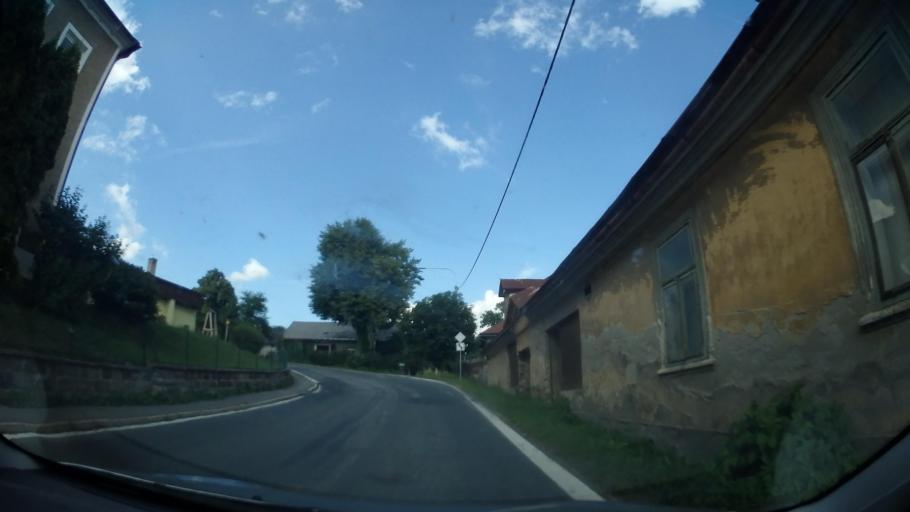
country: CZ
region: Vysocina
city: Zd'ar nad Sazavou Druhy
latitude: 49.6212
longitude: 15.9562
